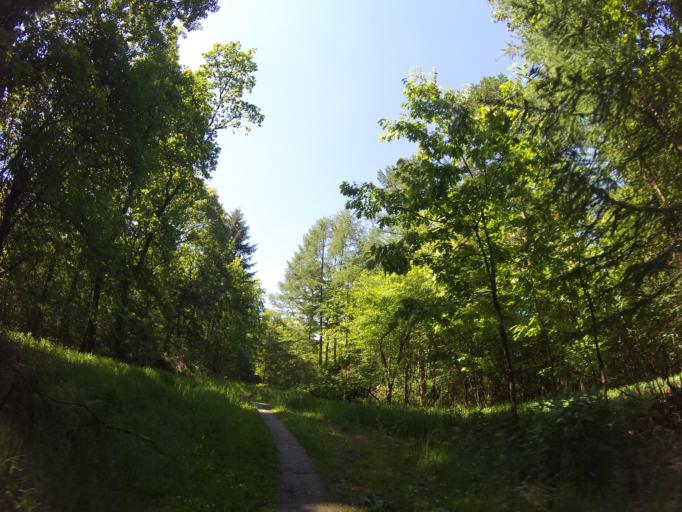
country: NL
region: Drenthe
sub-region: Gemeente Coevorden
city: Dalen
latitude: 52.7769
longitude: 6.6457
